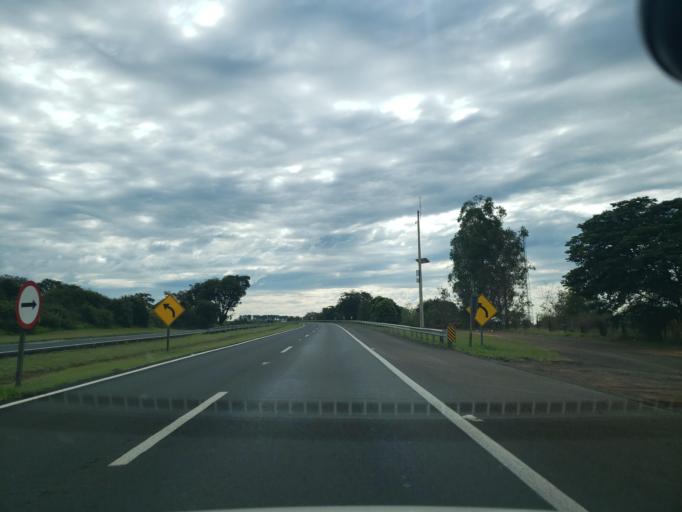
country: BR
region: Sao Paulo
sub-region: Bauru
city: Bauru
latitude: -22.1996
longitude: -49.1869
